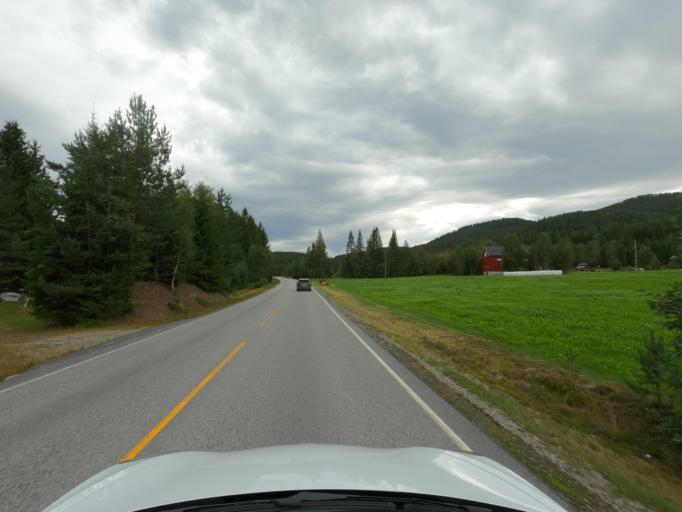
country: NO
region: Telemark
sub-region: Hjartdal
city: Sauland
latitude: 59.7024
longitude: 9.0124
